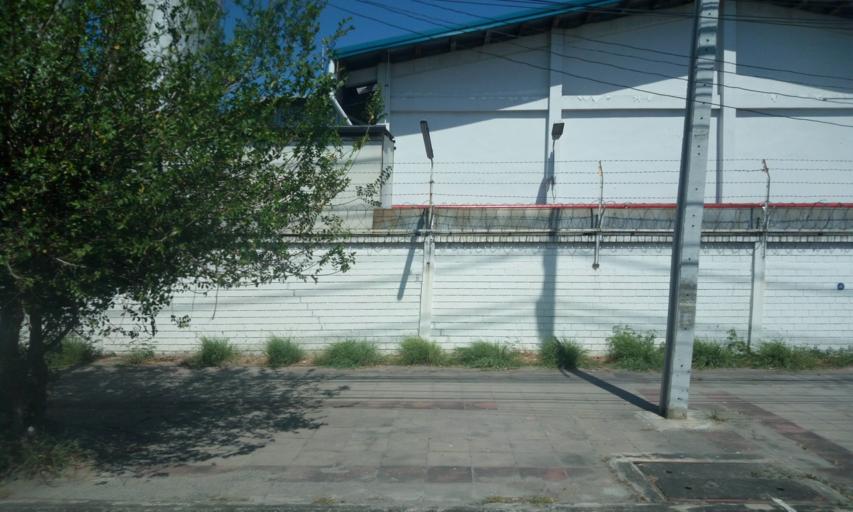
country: TH
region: Samut Prakan
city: Bang Bo District
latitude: 13.5711
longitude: 100.7932
